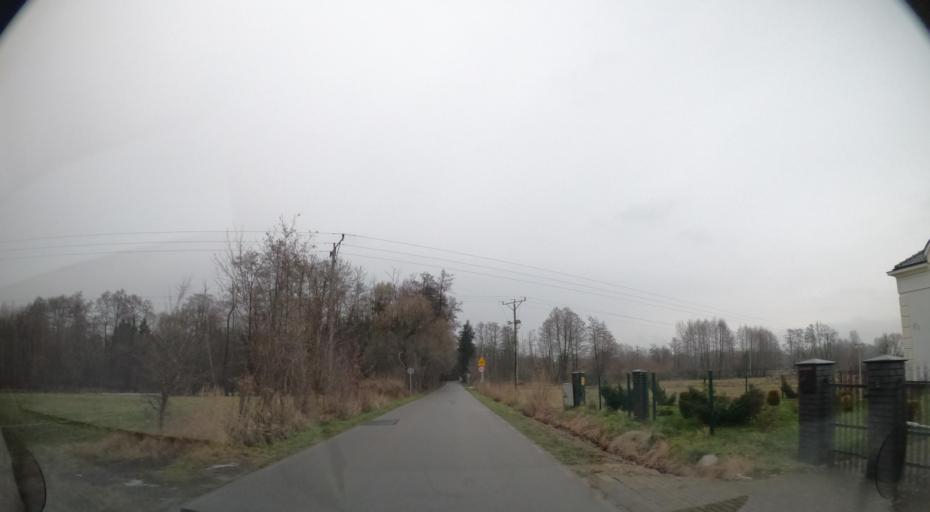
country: PL
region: Masovian Voivodeship
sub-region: Powiat radomski
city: Jastrzebia
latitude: 51.4227
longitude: 21.2268
